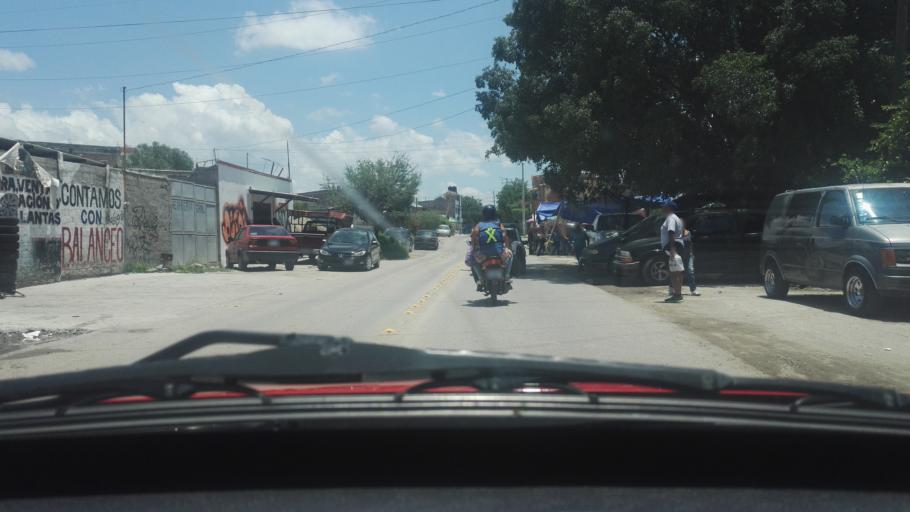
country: MX
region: Guanajuato
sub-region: Leon
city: San Jose de Duran (Los Troncoso)
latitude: 21.0856
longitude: -101.6302
